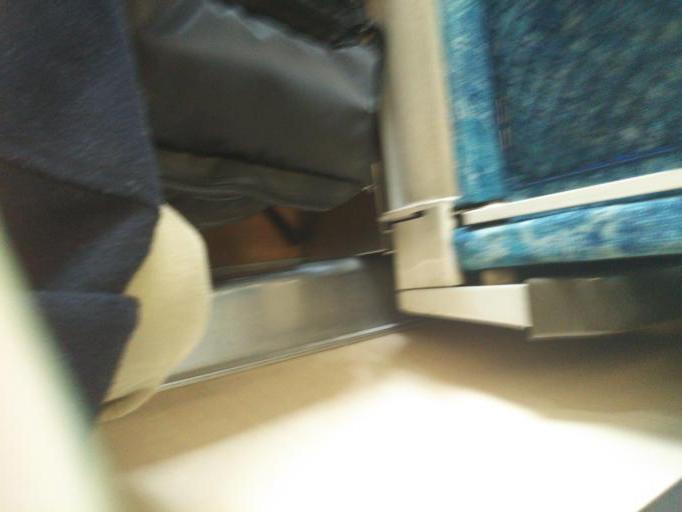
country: JP
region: Kagawa
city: Sakaidecho
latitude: 34.4265
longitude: 133.8049
